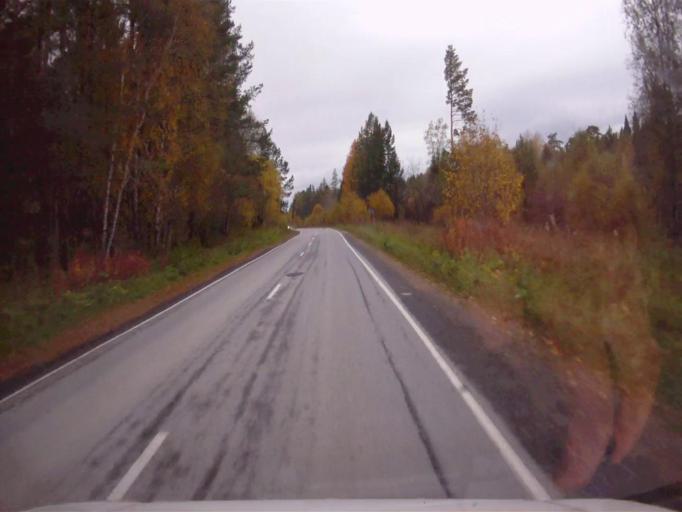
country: RU
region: Chelyabinsk
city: Nyazepetrovsk
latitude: 56.0520
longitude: 59.4844
